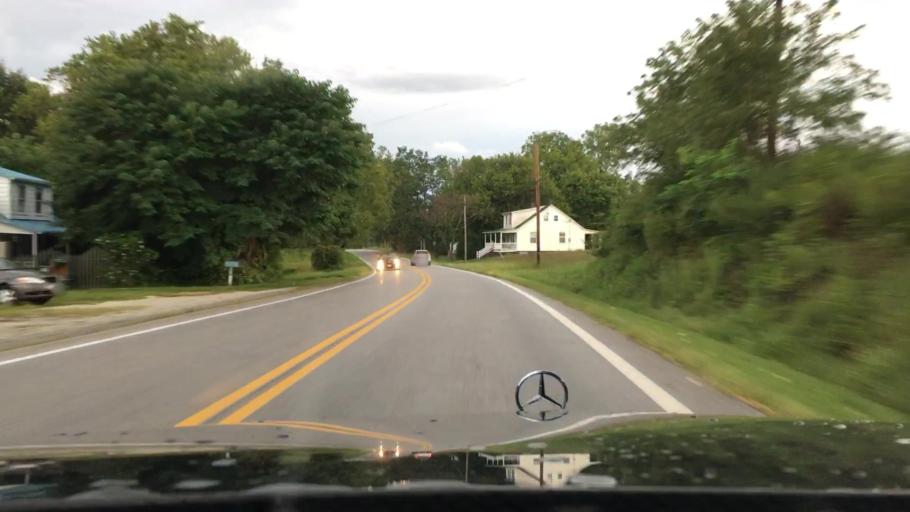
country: US
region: Virginia
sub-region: Amherst County
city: Amherst
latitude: 37.6417
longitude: -79.0226
